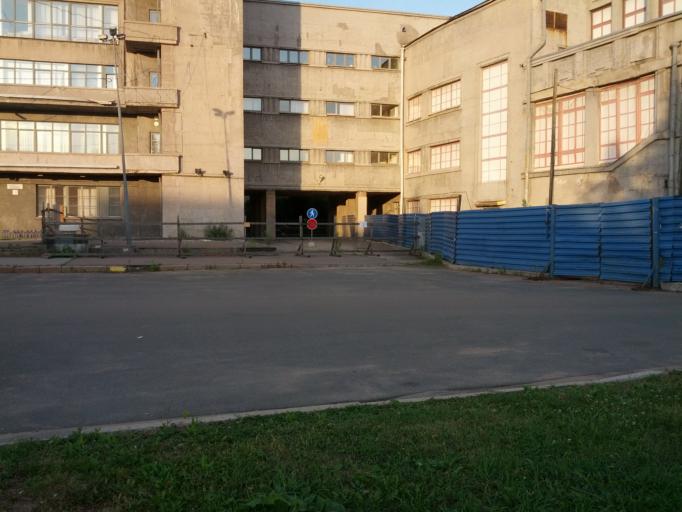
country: RU
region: St.-Petersburg
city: Admiralteisky
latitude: 59.8944
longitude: 30.2765
